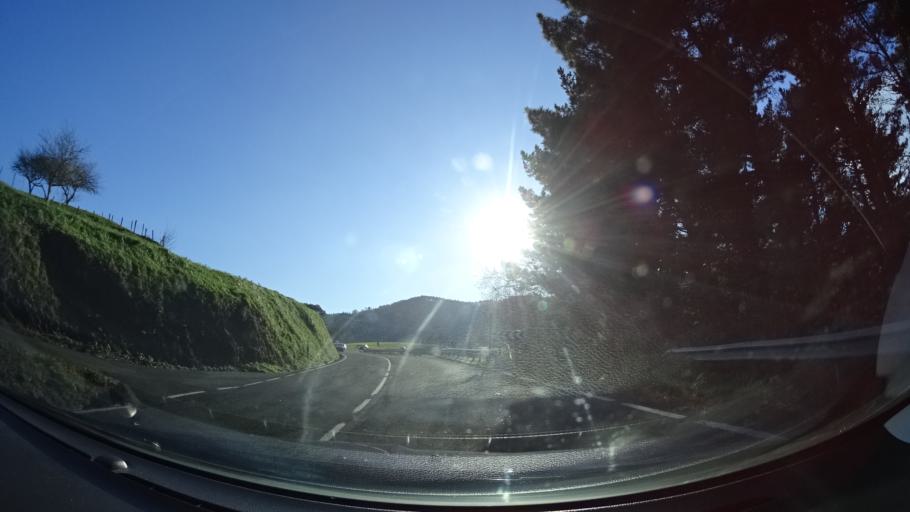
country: ES
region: Basque Country
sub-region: Bizkaia
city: Bermeo
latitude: 43.4146
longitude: -2.7535
